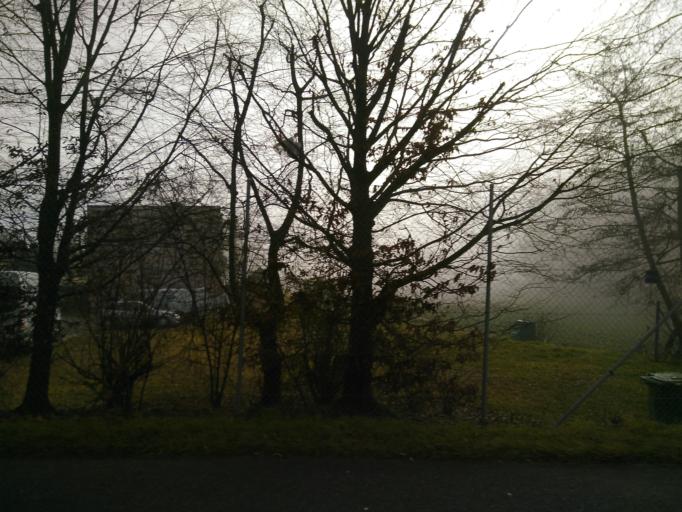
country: CH
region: Zurich
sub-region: Bezirk Hinwil
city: Gruet
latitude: 47.3093
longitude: 8.7777
